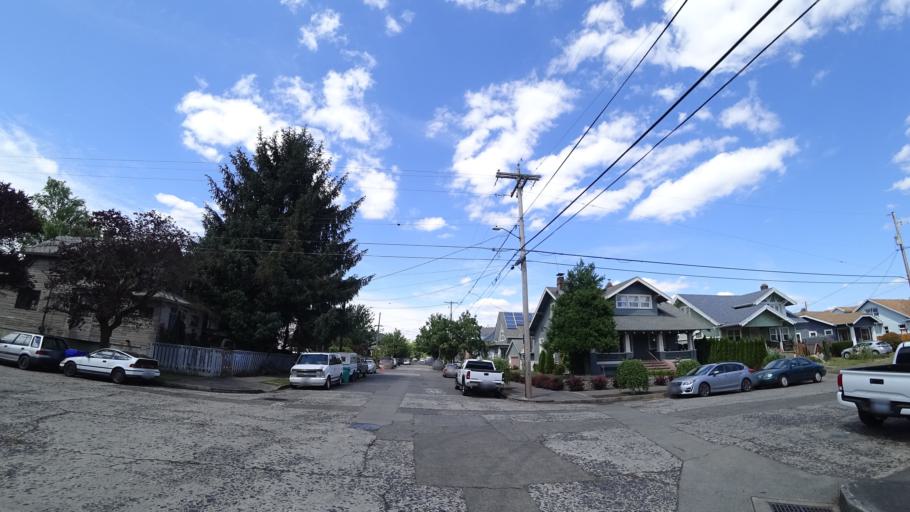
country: US
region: Oregon
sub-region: Multnomah County
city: Portland
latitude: 45.5611
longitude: -122.6770
